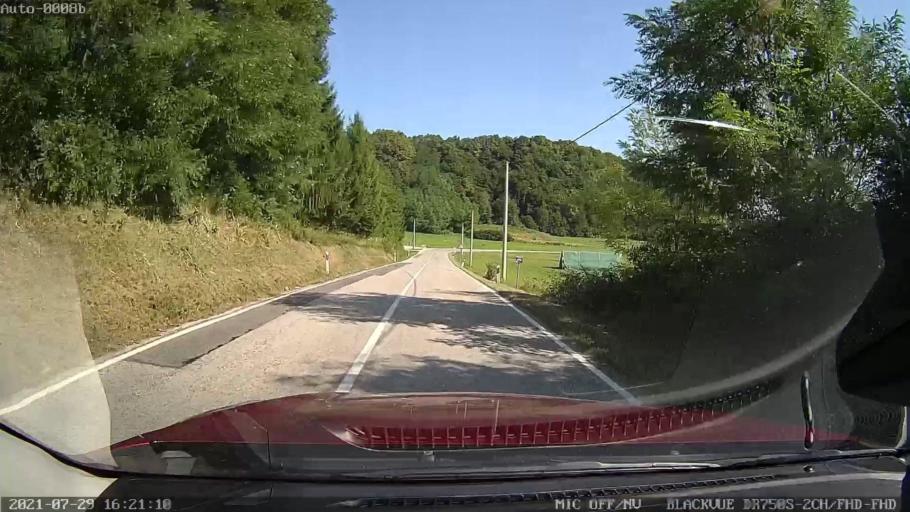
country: HR
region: Varazdinska
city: Lepoglava
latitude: 46.2365
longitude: 15.9658
